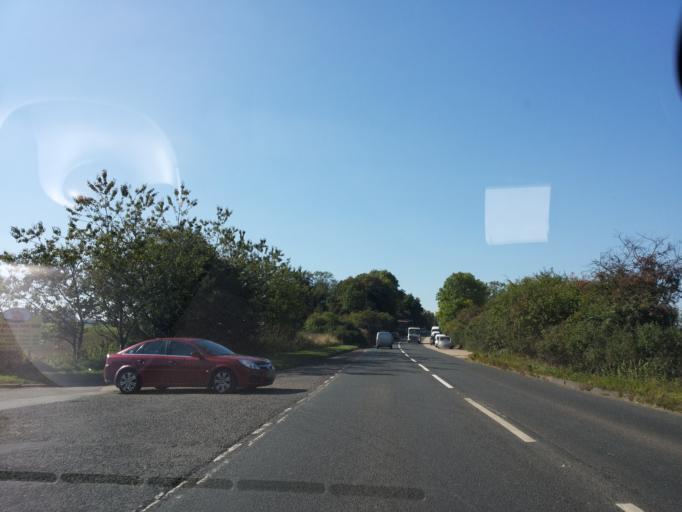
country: GB
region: England
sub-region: Doncaster
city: Marr
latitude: 53.5422
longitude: -1.2098
